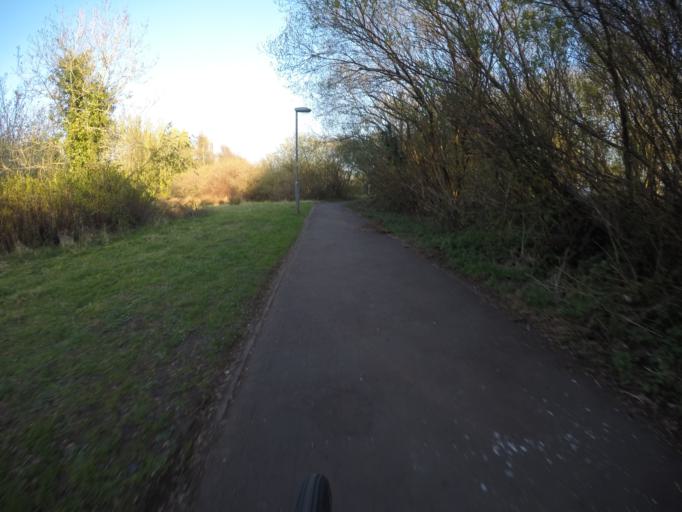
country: GB
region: Scotland
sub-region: North Ayrshire
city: Kilwinning
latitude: 55.6480
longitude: -4.6966
